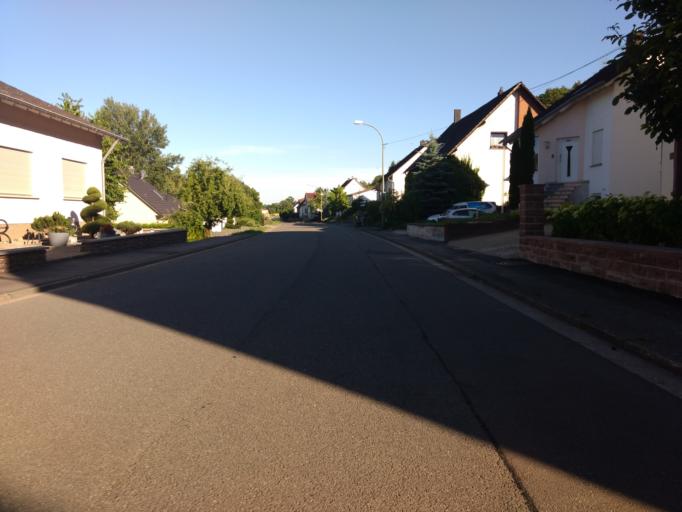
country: DE
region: Saarland
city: Merzig
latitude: 49.4162
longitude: 6.6320
